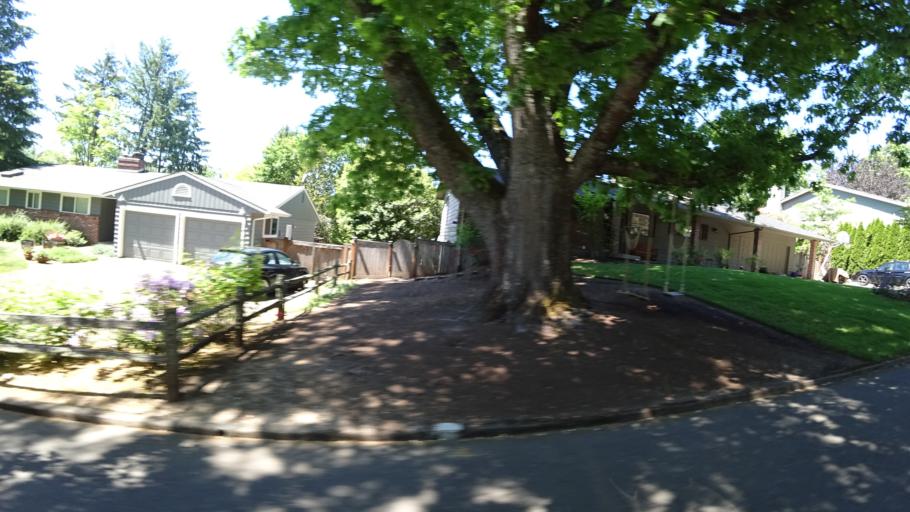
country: US
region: Oregon
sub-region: Washington County
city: Raleigh Hills
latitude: 45.4937
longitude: -122.7212
